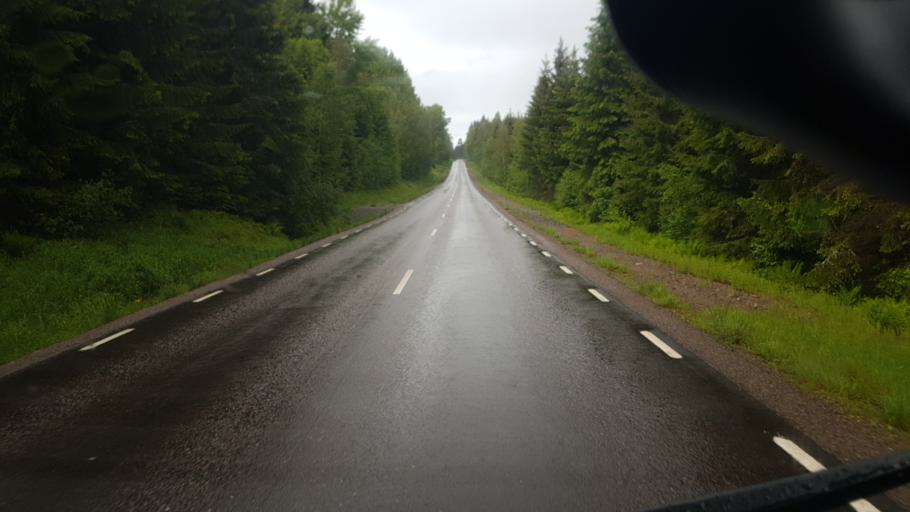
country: SE
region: Vaermland
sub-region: Eda Kommun
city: Amotfors
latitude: 59.7235
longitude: 12.4256
